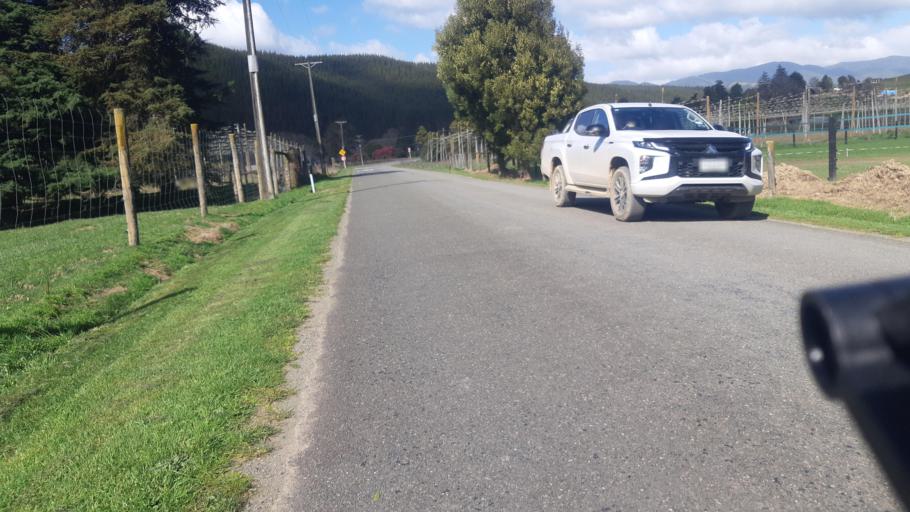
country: NZ
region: Tasman
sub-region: Tasman District
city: Wakefield
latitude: -41.4465
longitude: 172.9648
